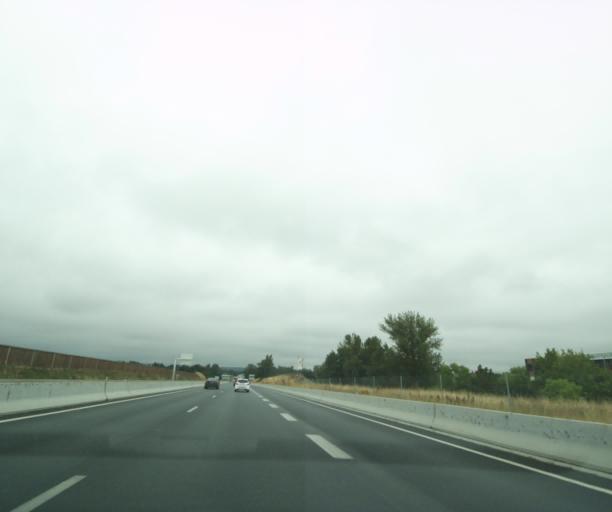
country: FR
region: Midi-Pyrenees
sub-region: Departement du Tarn
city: Albi
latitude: 43.9228
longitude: 2.1695
